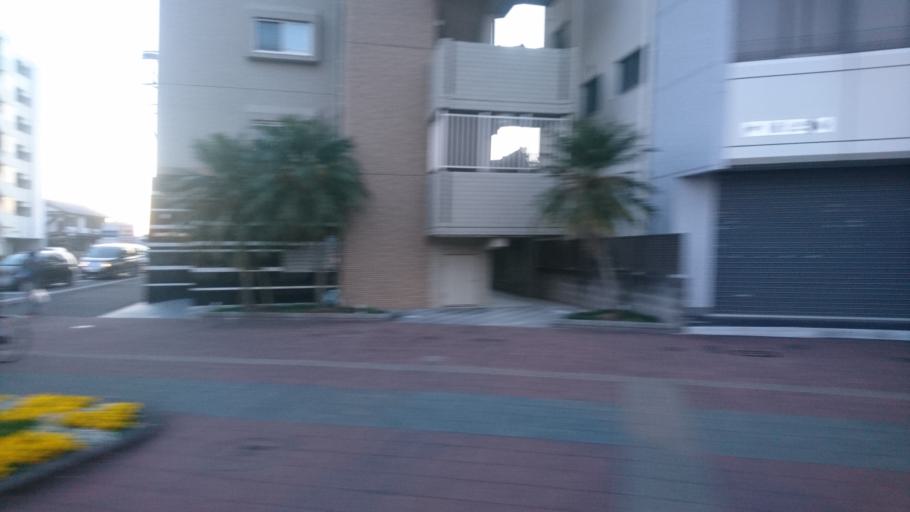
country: JP
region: Miyazaki
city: Miyazaki-shi
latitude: 31.8982
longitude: 131.4179
